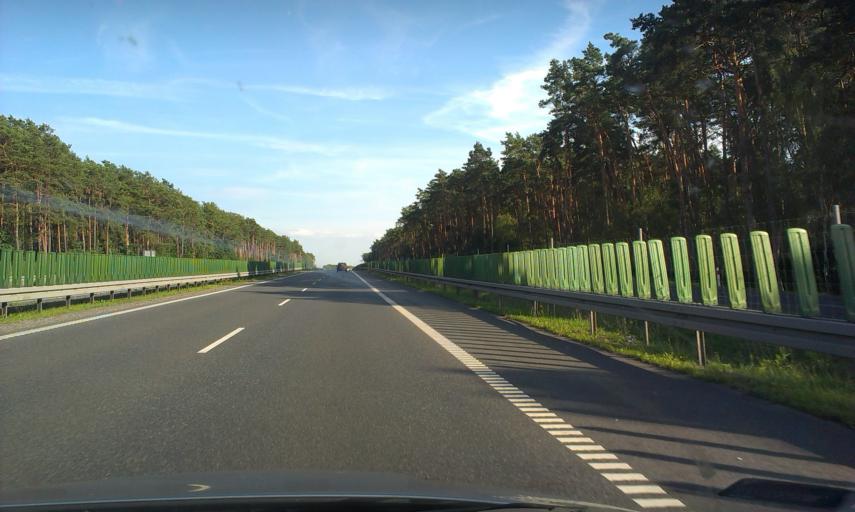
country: PL
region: Kujawsko-Pomorskie
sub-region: Powiat bydgoski
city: Biale Blota
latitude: 53.0840
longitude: 17.9067
